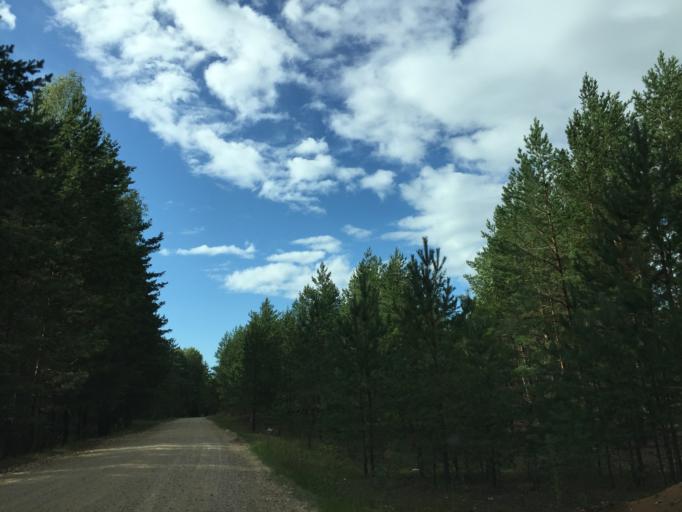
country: LV
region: Saulkrastu
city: Saulkrasti
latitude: 57.1815
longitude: 24.3779
